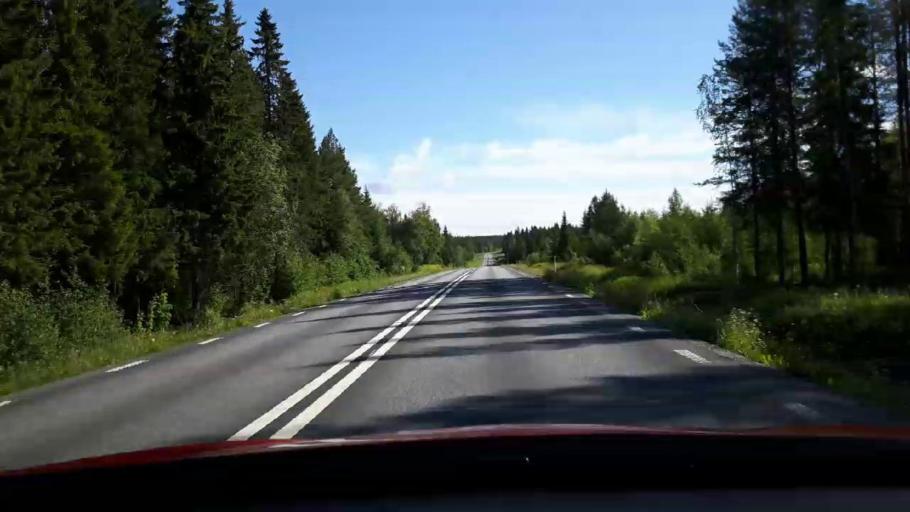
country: SE
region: Jaemtland
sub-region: OEstersunds Kommun
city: Ostersund
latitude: 63.2206
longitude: 14.7368
